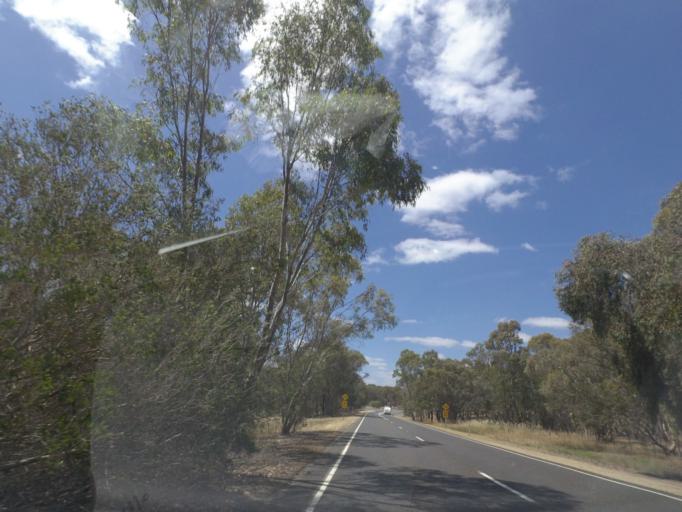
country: AU
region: Victoria
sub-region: Wangaratta
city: Wangaratta
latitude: -36.4651
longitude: 146.2144
